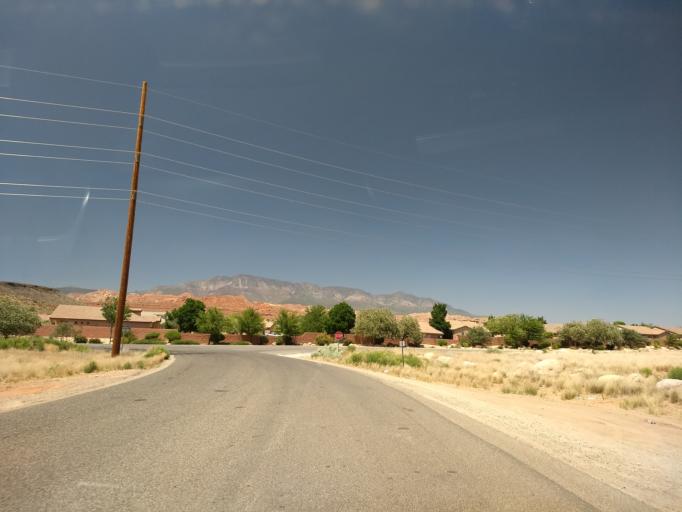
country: US
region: Utah
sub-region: Washington County
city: Washington
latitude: 37.1423
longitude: -113.4575
